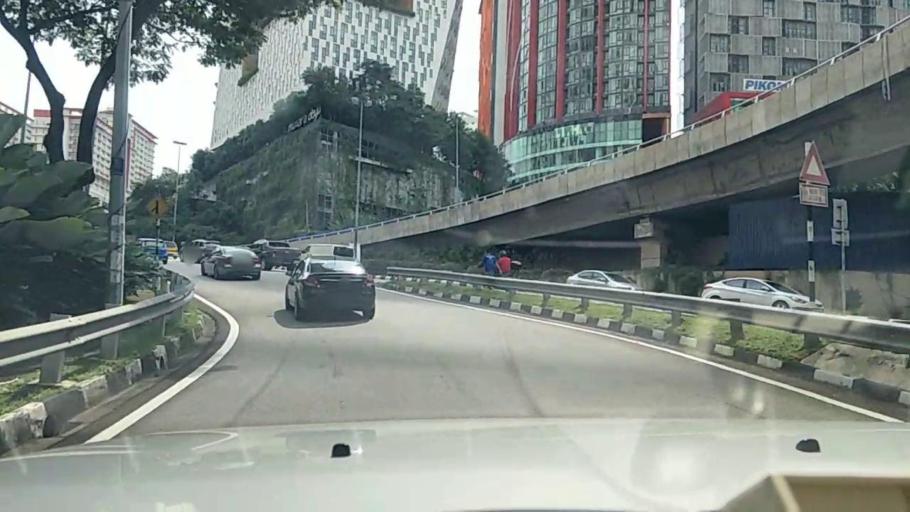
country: MY
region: Selangor
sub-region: Petaling
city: Petaling Jaya
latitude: 3.1655
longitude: 101.6139
